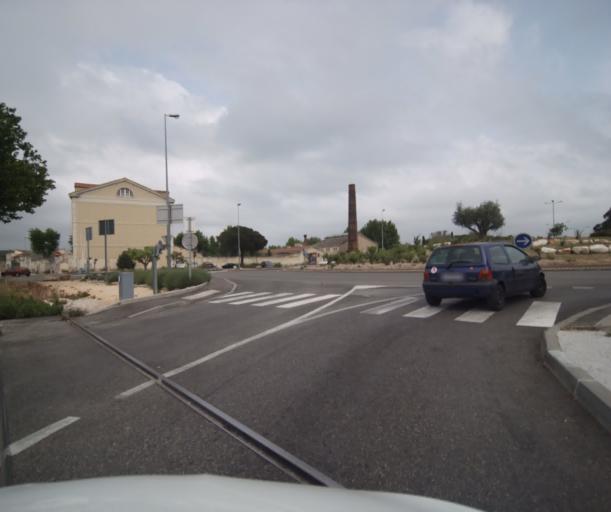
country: FR
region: Provence-Alpes-Cote d'Azur
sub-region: Departement du Var
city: La Seyne-sur-Mer
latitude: 43.1185
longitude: 5.8833
